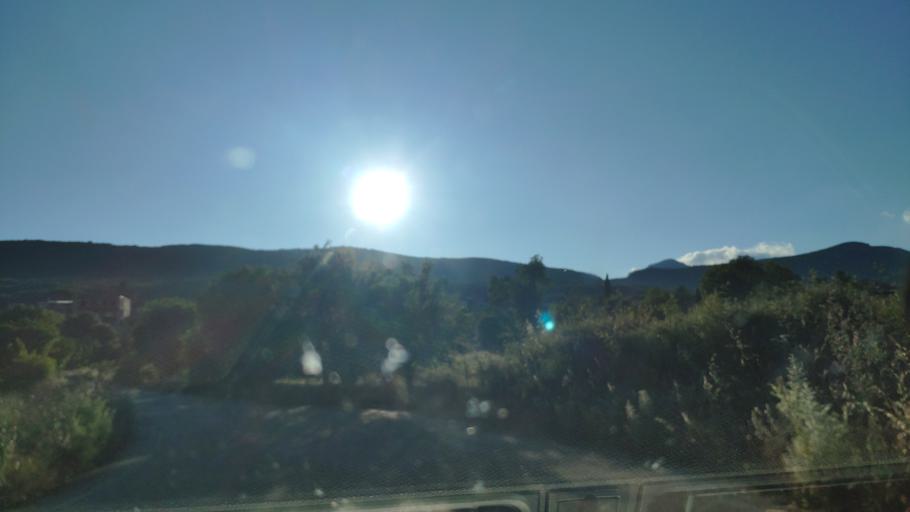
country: GR
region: West Greece
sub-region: Nomos Aitolias kai Akarnanias
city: Fitiai
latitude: 38.6336
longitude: 21.1551
